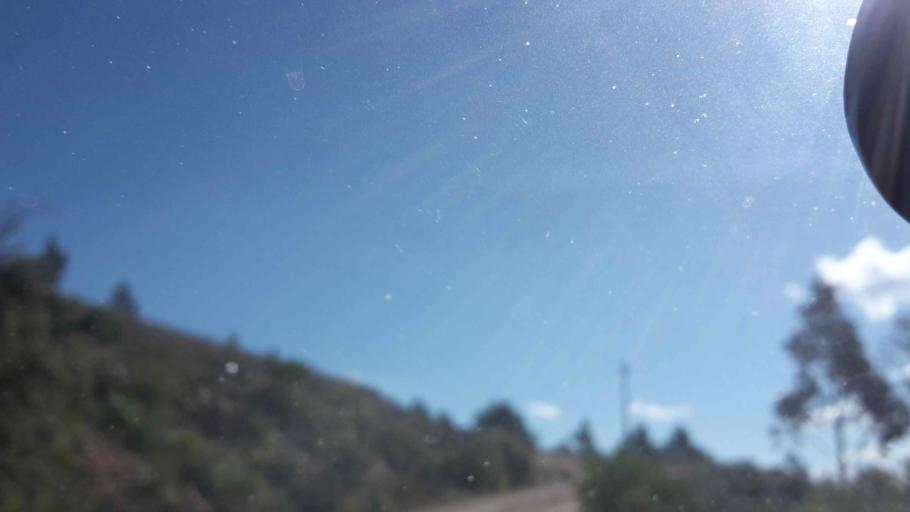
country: BO
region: Cochabamba
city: Arani
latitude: -17.6636
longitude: -65.7350
